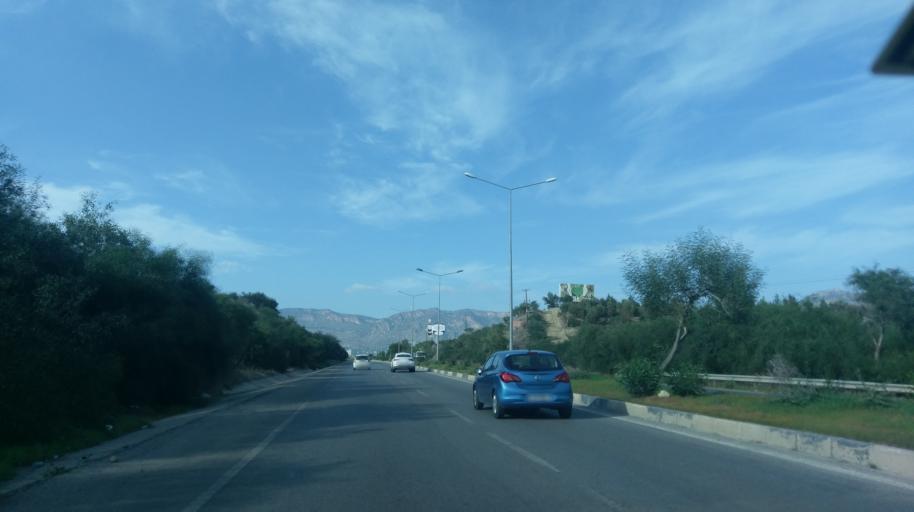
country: CY
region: Keryneia
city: Kyrenia
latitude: 35.2483
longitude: 33.3052
